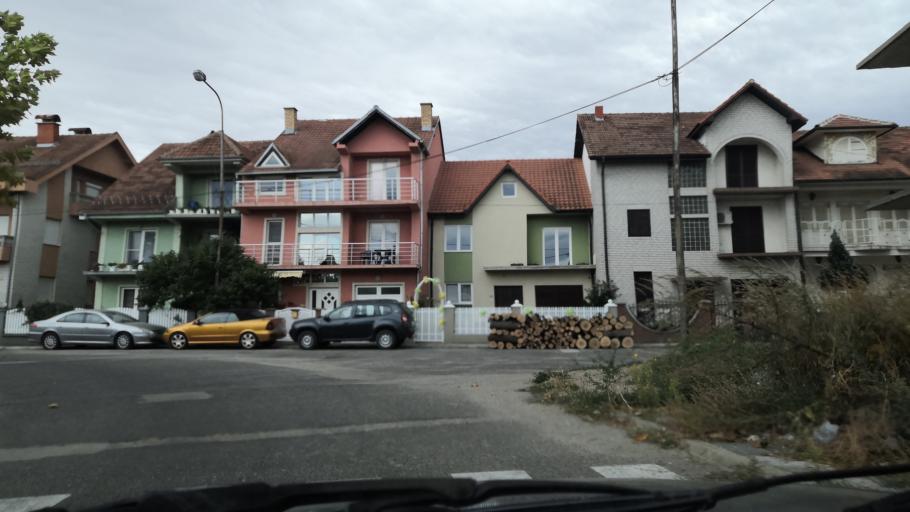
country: RS
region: Central Serbia
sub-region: Borski Okrug
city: Negotin
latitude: 44.2282
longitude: 22.5237
